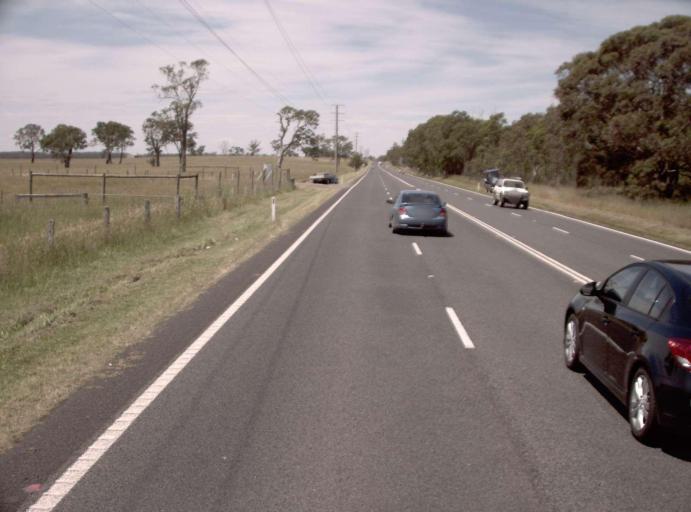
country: AU
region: Victoria
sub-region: Latrobe
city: Traralgon
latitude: -38.1781
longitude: 146.6339
